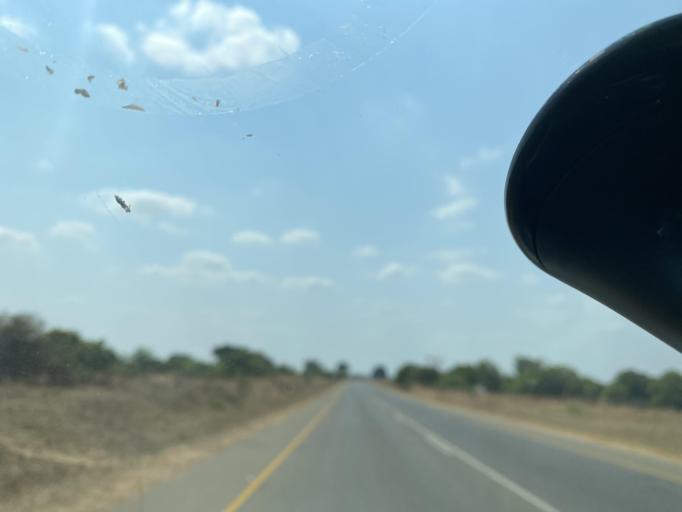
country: ZM
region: Lusaka
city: Chongwe
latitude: -15.5874
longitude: 28.7098
